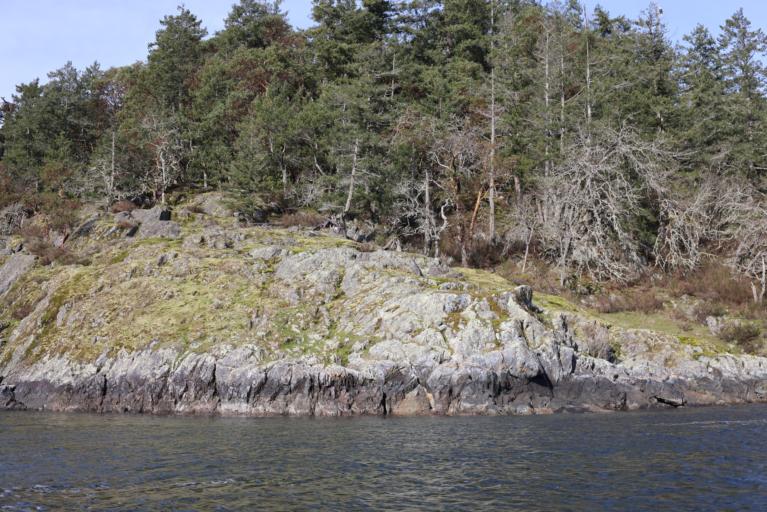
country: CA
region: British Columbia
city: North Cowichan
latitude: 48.7795
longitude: -123.5589
